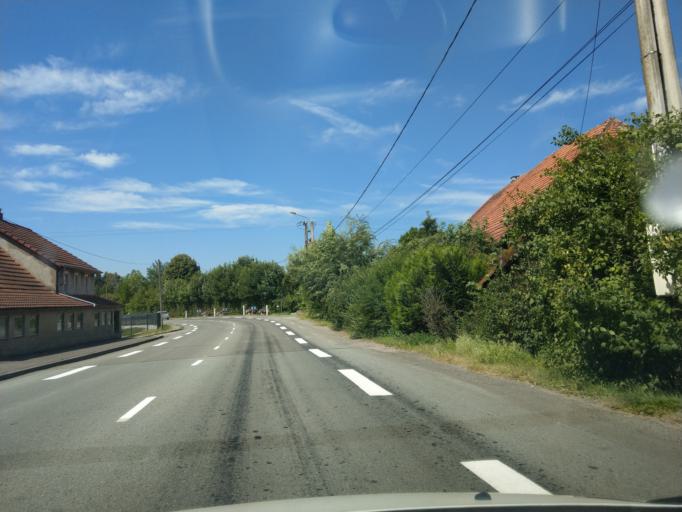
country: FR
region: Franche-Comte
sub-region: Territoire de Belfort
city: Chevremont
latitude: 47.6732
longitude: 6.9253
